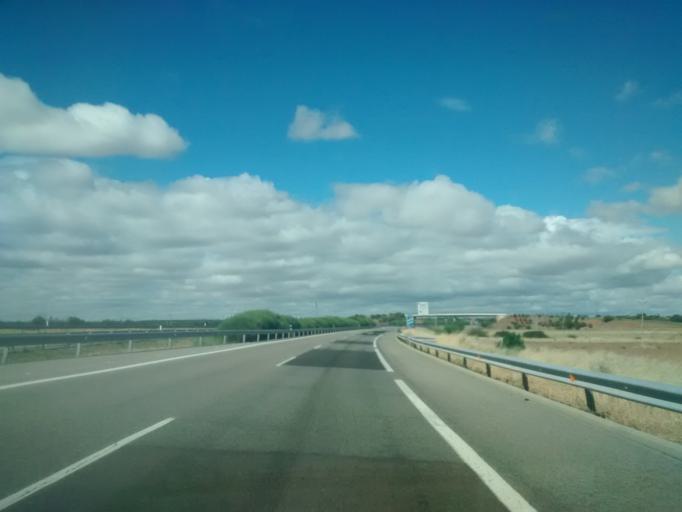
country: ES
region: Castille and Leon
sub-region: Provincia de Salamanca
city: Doninos de Salamanca
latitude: 40.9365
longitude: -5.7801
